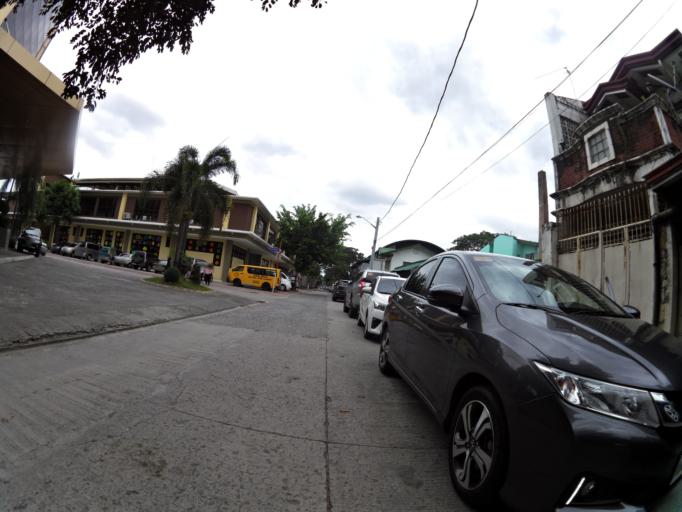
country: PH
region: Calabarzon
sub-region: Province of Rizal
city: Antipolo
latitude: 14.6373
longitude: 121.1112
